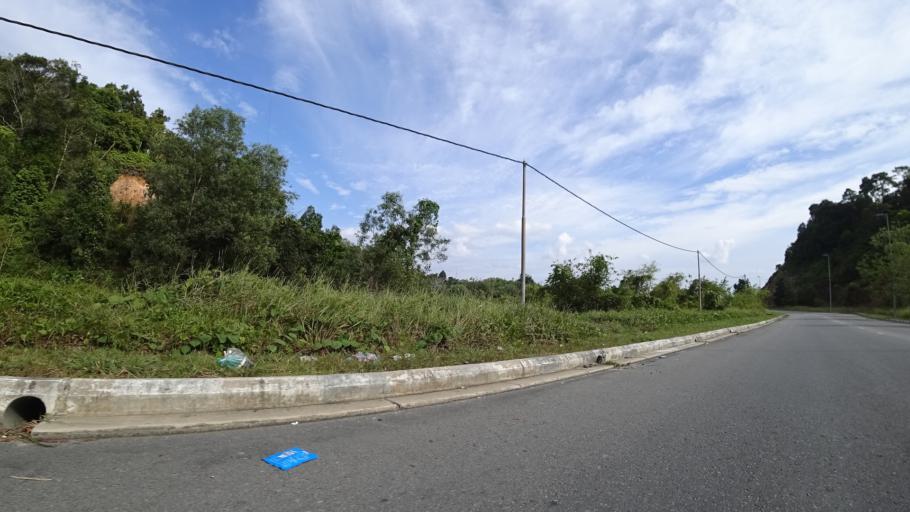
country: BN
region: Brunei and Muara
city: Bandar Seri Begawan
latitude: 4.8869
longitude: 114.8031
